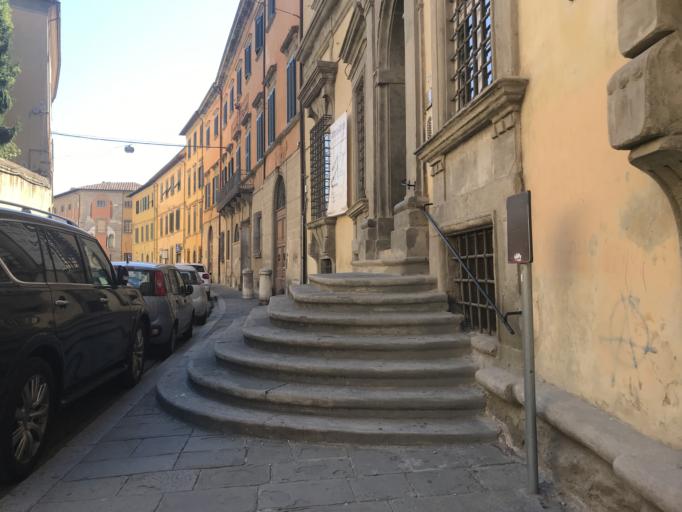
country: IT
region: Tuscany
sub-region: Province of Pisa
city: Pisa
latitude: 43.7176
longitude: 10.3965
